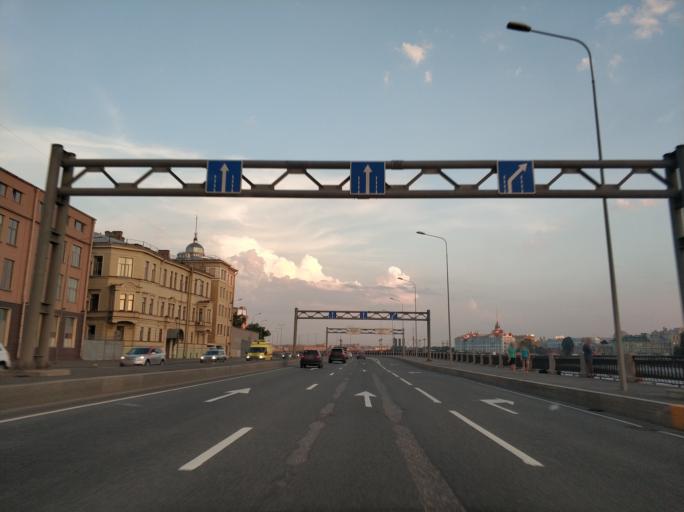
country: RU
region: Leningrad
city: Sampsonievskiy
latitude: 59.9616
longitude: 30.3380
